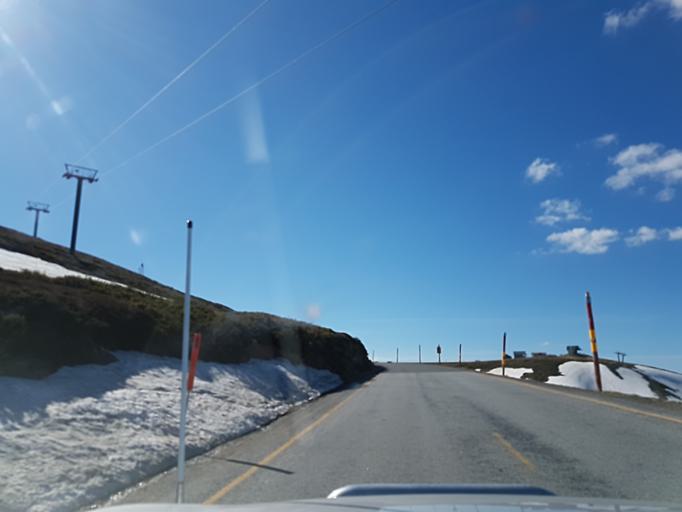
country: AU
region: Victoria
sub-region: Alpine
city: Mount Beauty
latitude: -36.9787
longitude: 147.1415
